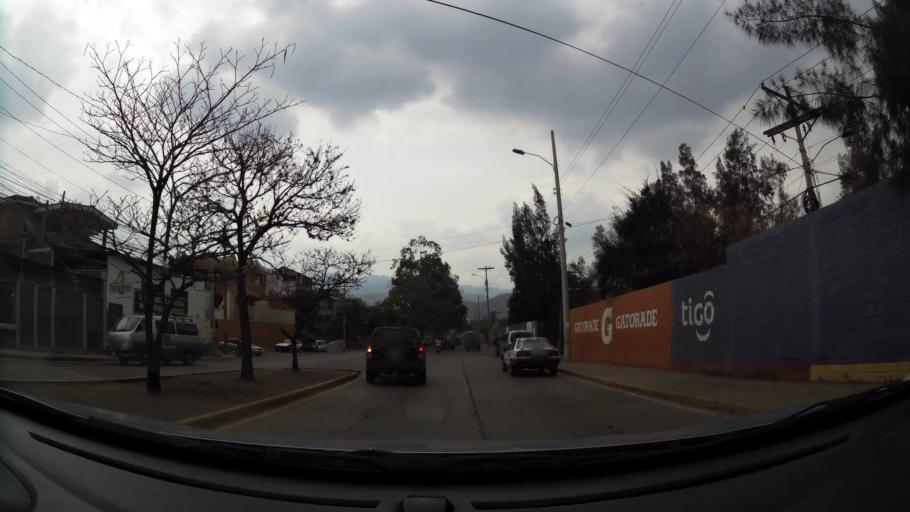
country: HN
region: Francisco Morazan
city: Tegucigalpa
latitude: 14.0919
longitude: -87.1640
